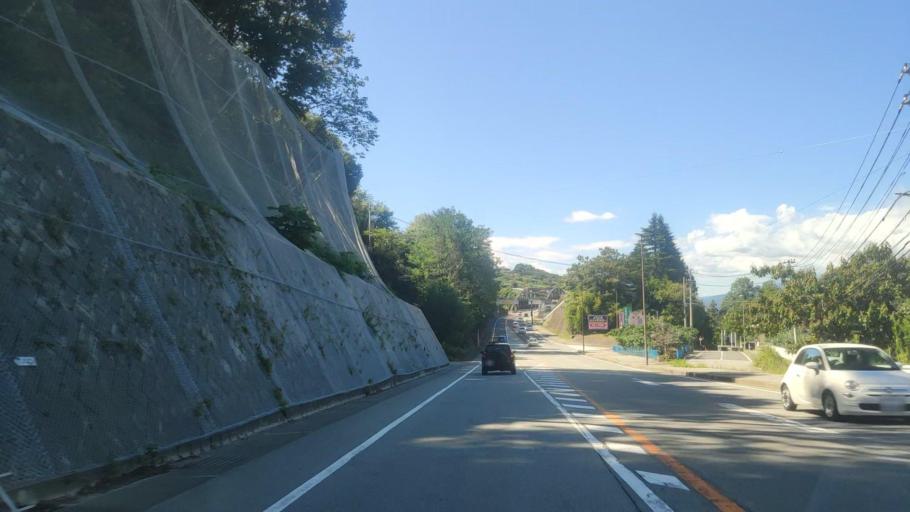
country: JP
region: Yamanashi
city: Isawa
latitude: 35.5941
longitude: 138.7160
